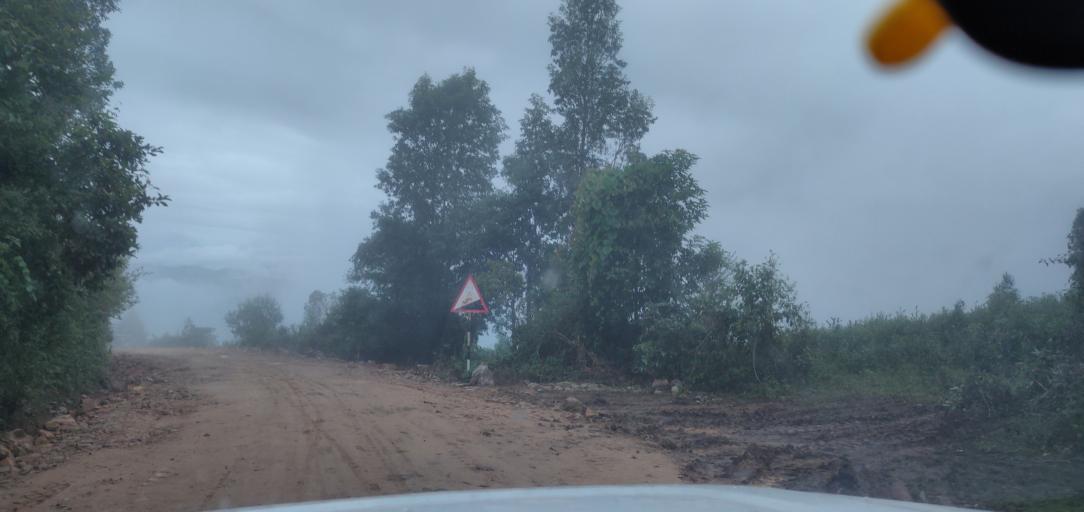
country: LA
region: Phongsali
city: Phongsali
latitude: 21.4278
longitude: 102.2625
